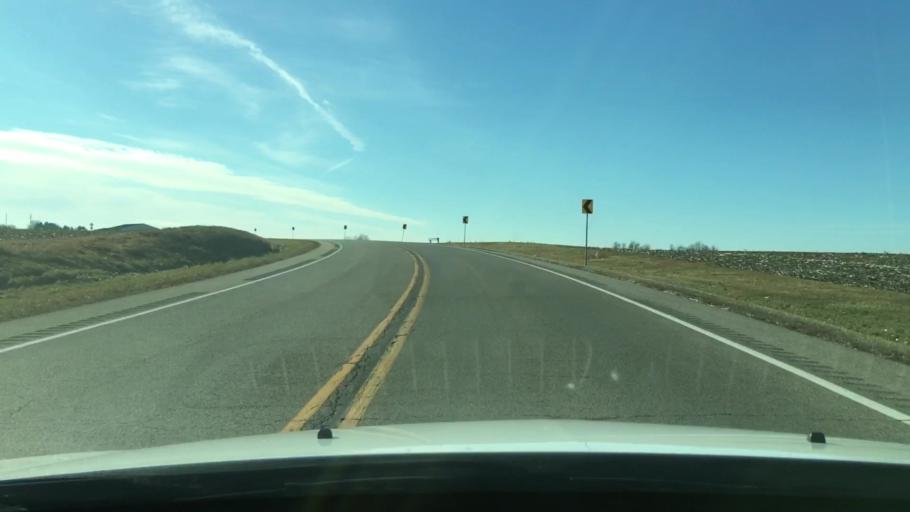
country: US
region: Illinois
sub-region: Woodford County
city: Washburn
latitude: 40.8627
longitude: -89.3312
